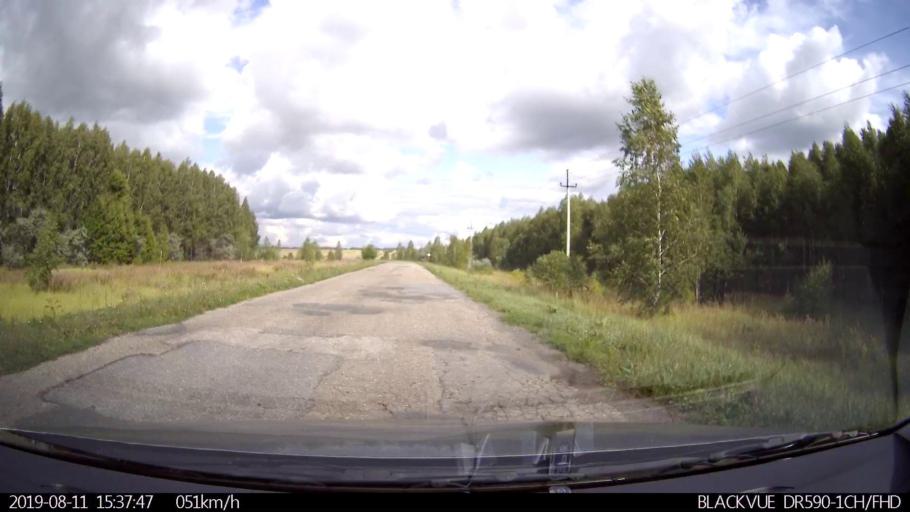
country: RU
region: Ulyanovsk
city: Ignatovka
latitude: 53.8587
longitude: 47.6367
